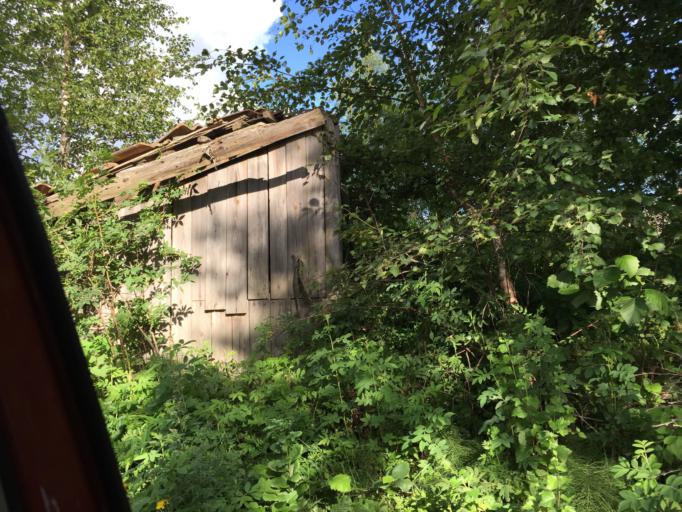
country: SE
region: Gaevleborg
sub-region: Ljusdals Kommun
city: Jaervsoe
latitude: 61.7561
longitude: 16.1679
